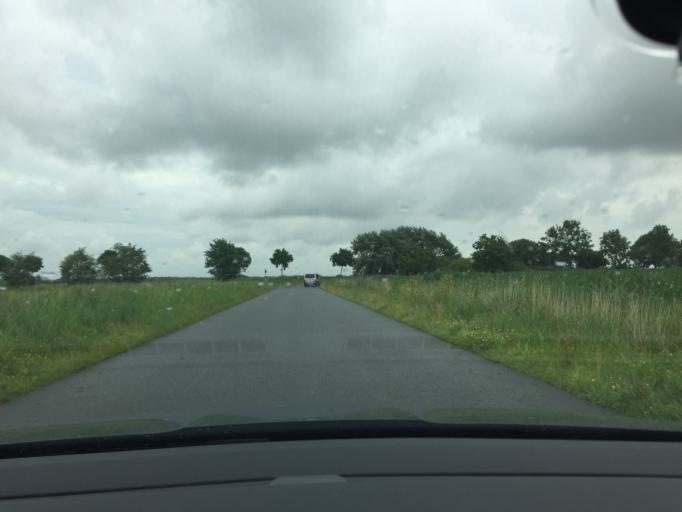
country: DE
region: Lower Saxony
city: Wirdum
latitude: 53.4955
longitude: 7.0662
